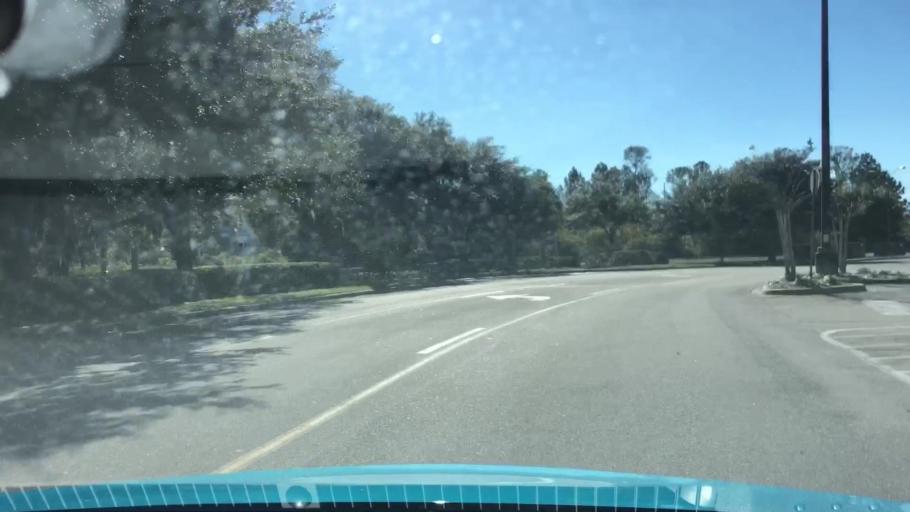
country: US
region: Florida
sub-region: Seminole County
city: Lake Mary
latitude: 28.8043
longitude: -81.3357
